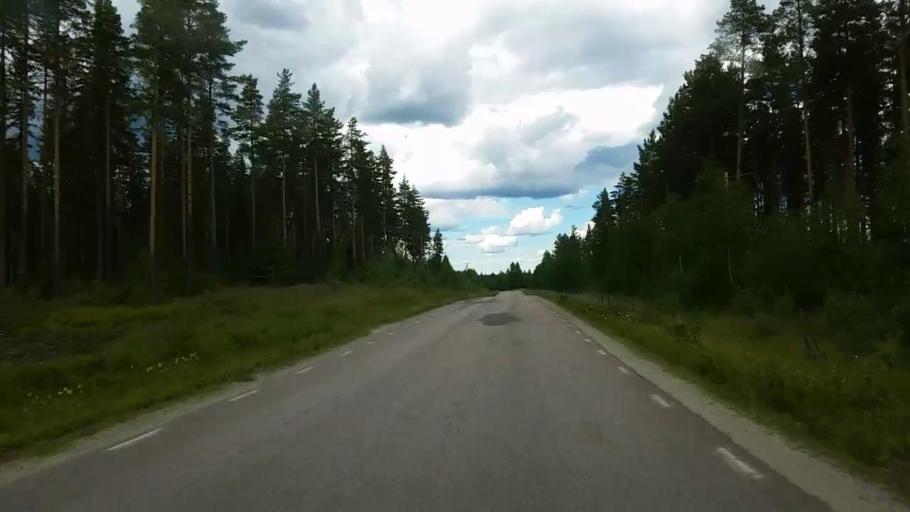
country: SE
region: Gaevleborg
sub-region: Ovanakers Kommun
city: Edsbyn
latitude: 61.4153
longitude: 15.8992
